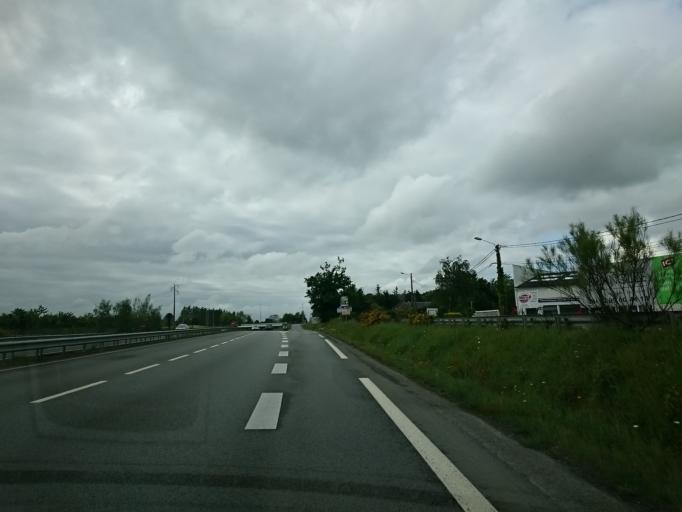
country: FR
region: Brittany
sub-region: Departement d'Ille-et-Vilaine
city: Vern-sur-Seiche
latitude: 48.0609
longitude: -1.6156
